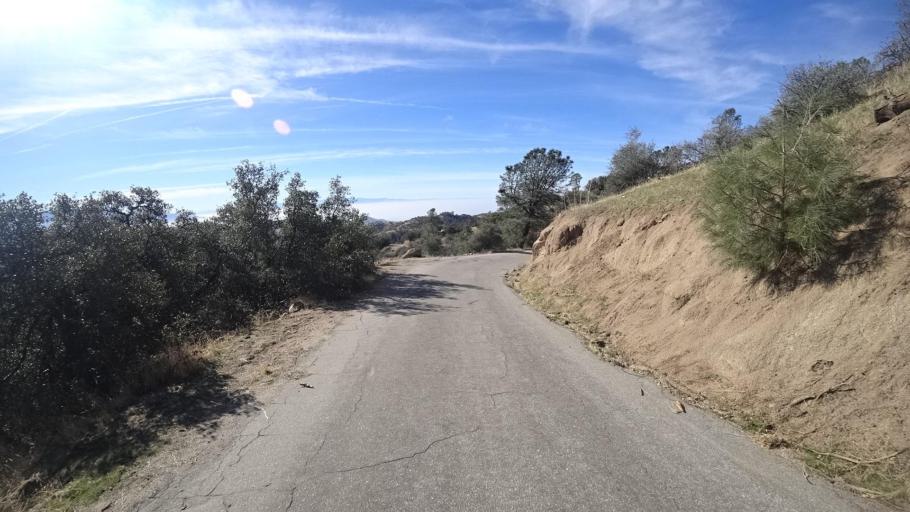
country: US
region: California
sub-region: Kern County
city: Bodfish
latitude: 35.4506
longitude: -118.6592
